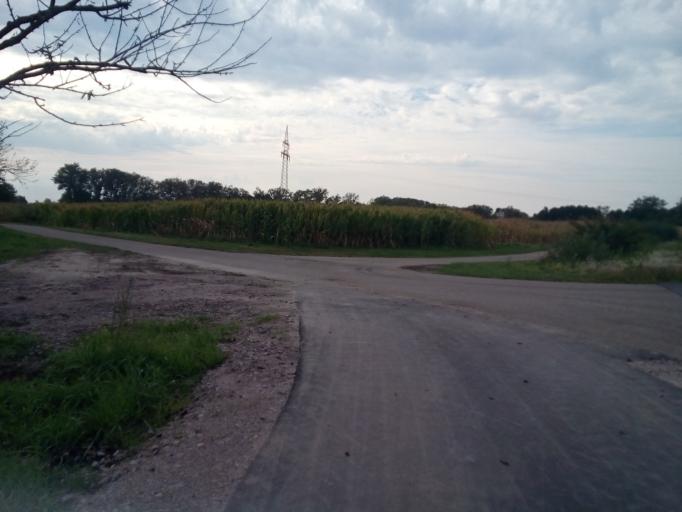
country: DE
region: Baden-Wuerttemberg
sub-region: Karlsruhe Region
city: Lichtenau
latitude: 48.6990
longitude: 7.9781
